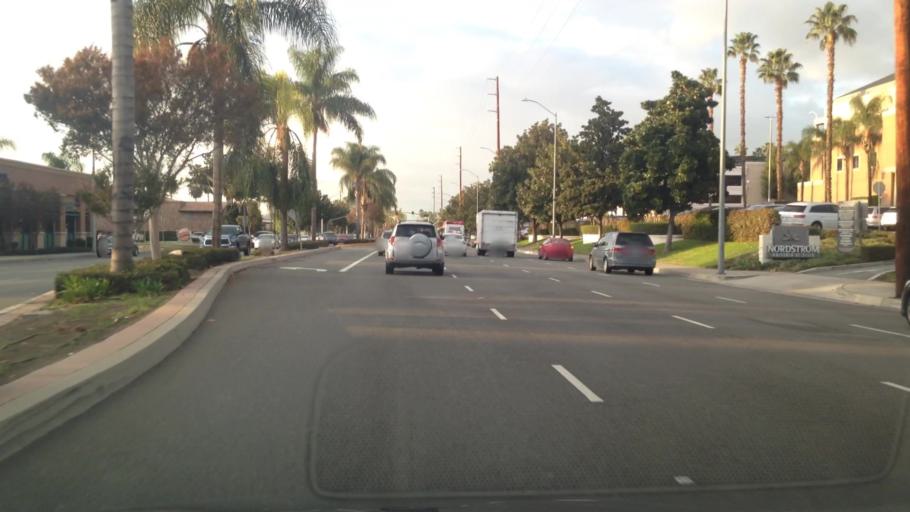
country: US
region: California
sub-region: Riverside County
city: Pedley
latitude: 33.9085
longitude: -117.4586
